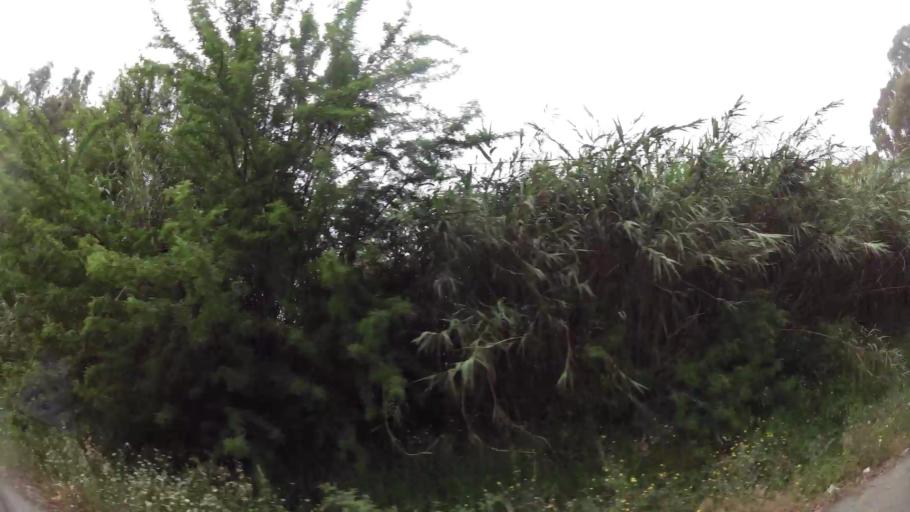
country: MA
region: Rabat-Sale-Zemmour-Zaer
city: Sale
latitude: 33.9949
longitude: -6.7699
